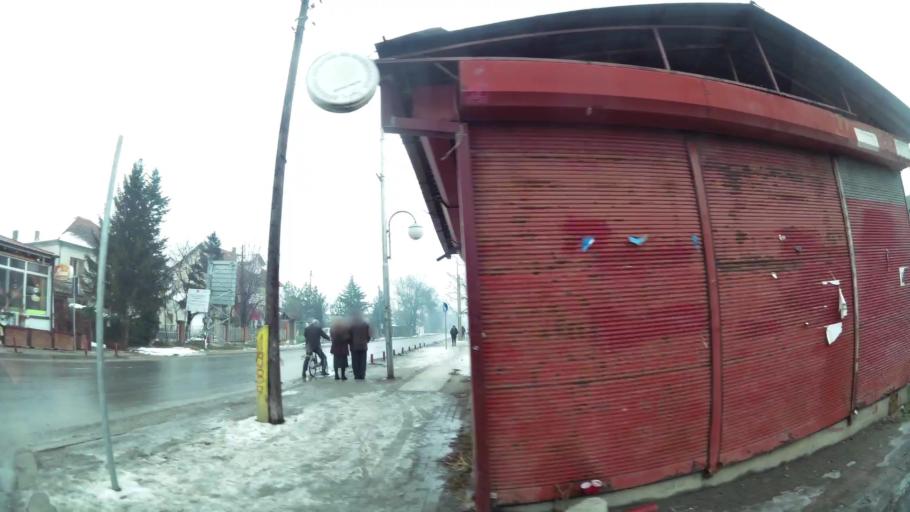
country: MK
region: Petrovec
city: Petrovec
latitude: 41.9374
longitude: 21.6179
